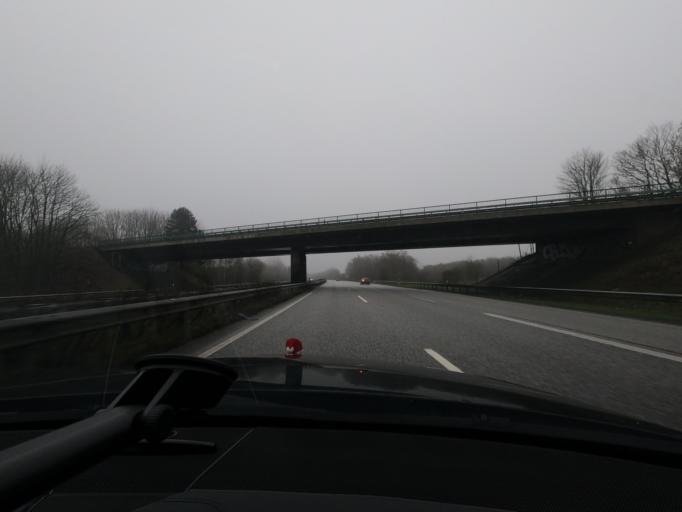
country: DE
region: Schleswig-Holstein
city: Busdorf
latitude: 54.4827
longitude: 9.5338
